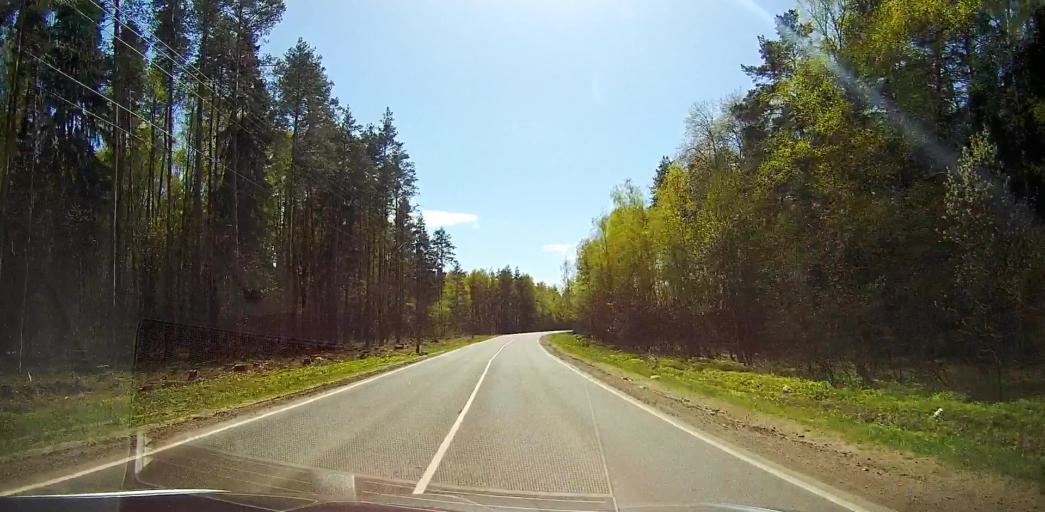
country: RU
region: Moskovskaya
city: Beloozerskiy
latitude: 55.4993
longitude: 38.4310
